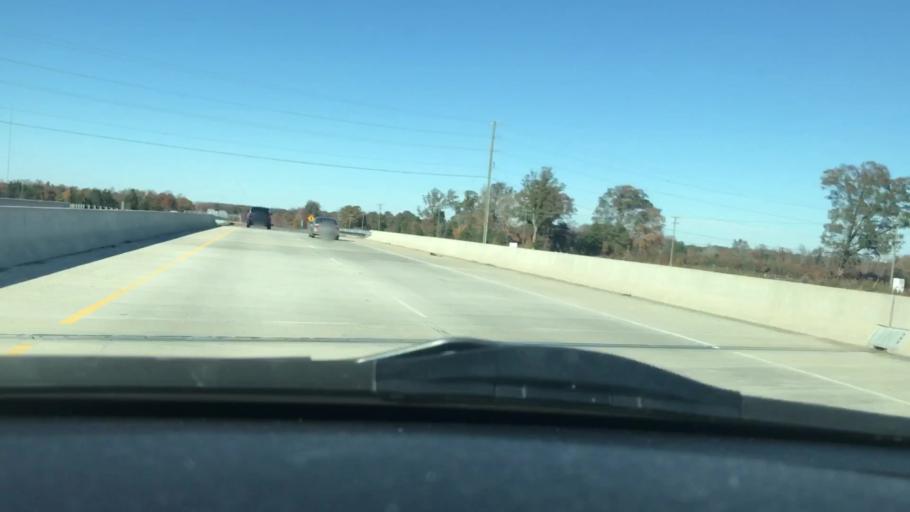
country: US
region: North Carolina
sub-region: Guilford County
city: Summerfield
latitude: 36.2466
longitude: -79.9209
